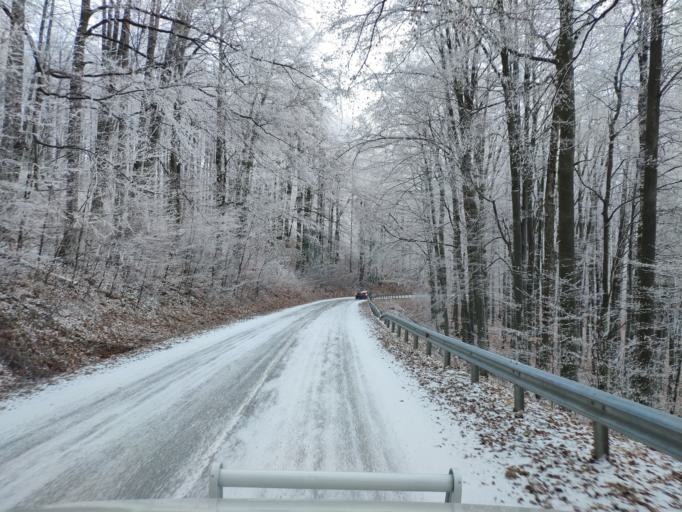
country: SK
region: Kosicky
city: Dobsina
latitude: 48.8028
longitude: 20.4923
